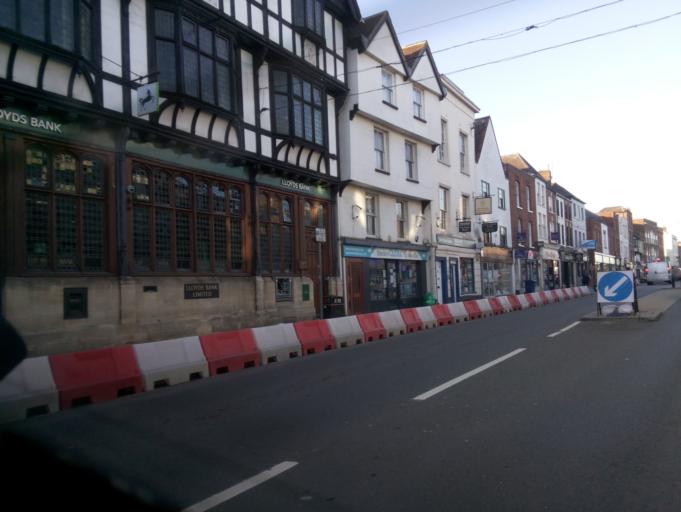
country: GB
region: England
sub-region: Gloucestershire
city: Tewkesbury
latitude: 51.9940
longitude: -2.1571
